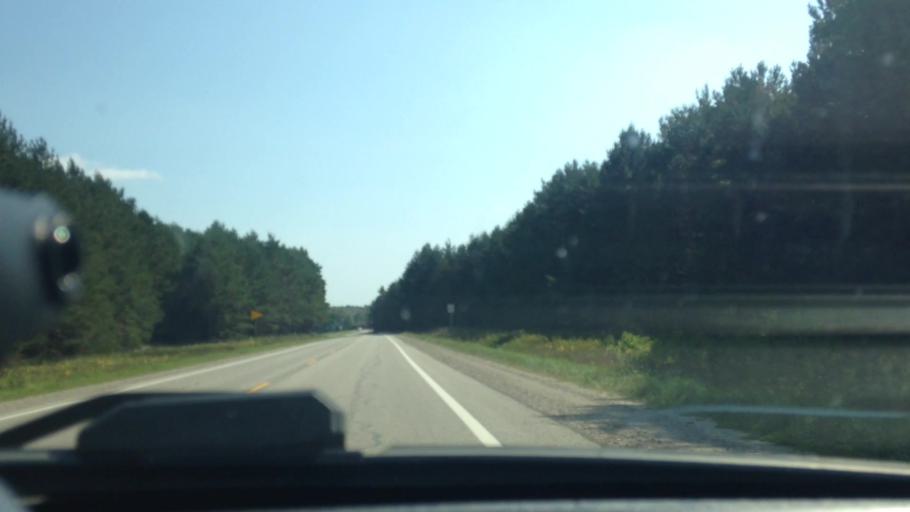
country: US
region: Michigan
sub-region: Luce County
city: Newberry
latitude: 46.3158
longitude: -85.6636
